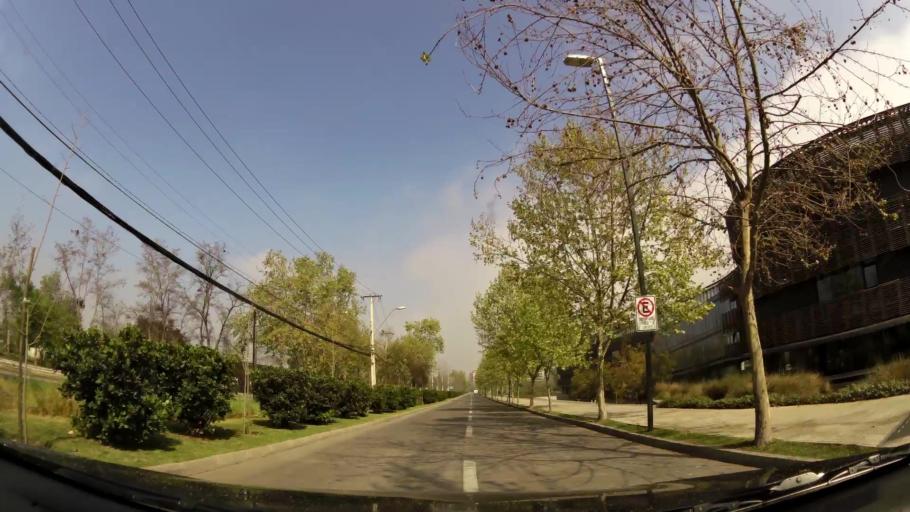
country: CL
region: Santiago Metropolitan
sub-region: Provincia de Santiago
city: Villa Presidente Frei, Nunoa, Santiago, Chile
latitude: -33.3799
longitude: -70.5837
